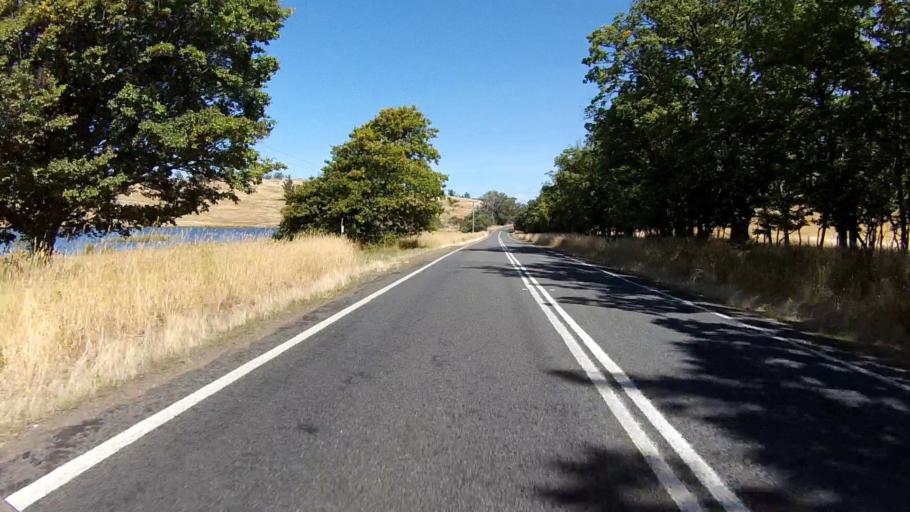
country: AU
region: Tasmania
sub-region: Sorell
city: Sorell
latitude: -42.4883
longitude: 147.9345
